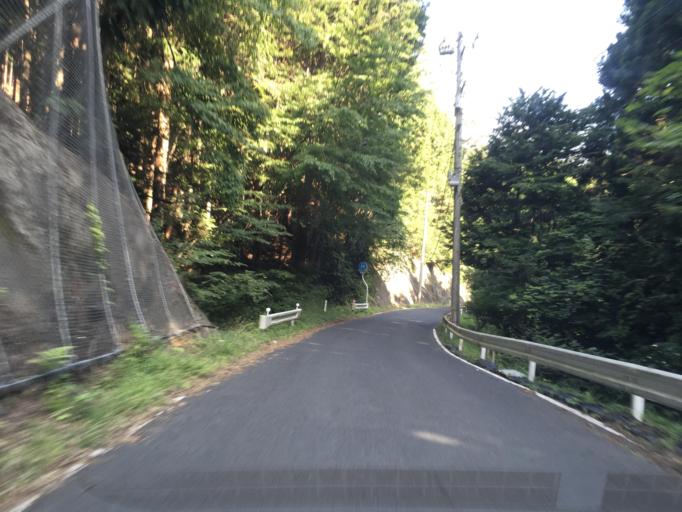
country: JP
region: Iwate
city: Ofunato
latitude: 38.9151
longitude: 141.6182
